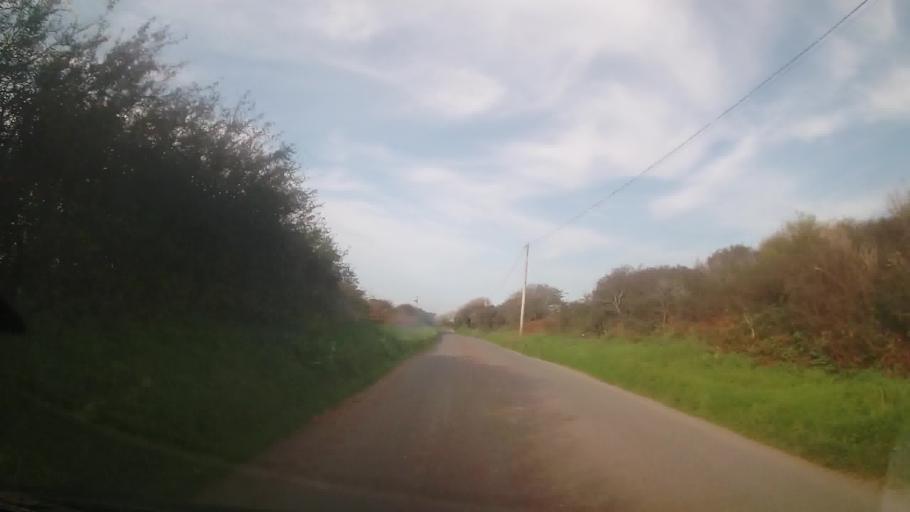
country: GB
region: Wales
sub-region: Pembrokeshire
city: Camrose
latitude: 51.8728
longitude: -5.0490
